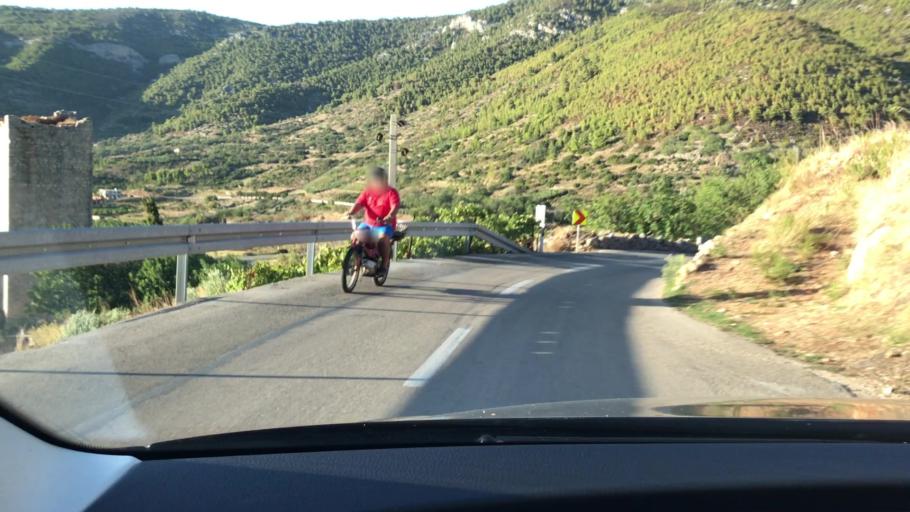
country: HR
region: Splitsko-Dalmatinska
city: Komiza
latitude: 43.0402
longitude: 16.0966
